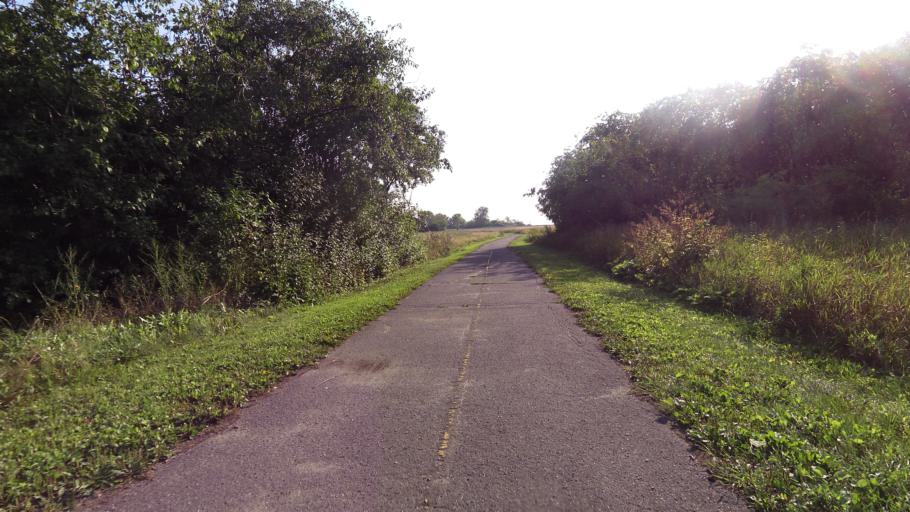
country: CA
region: Ontario
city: Ottawa
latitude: 45.3996
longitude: -75.7590
